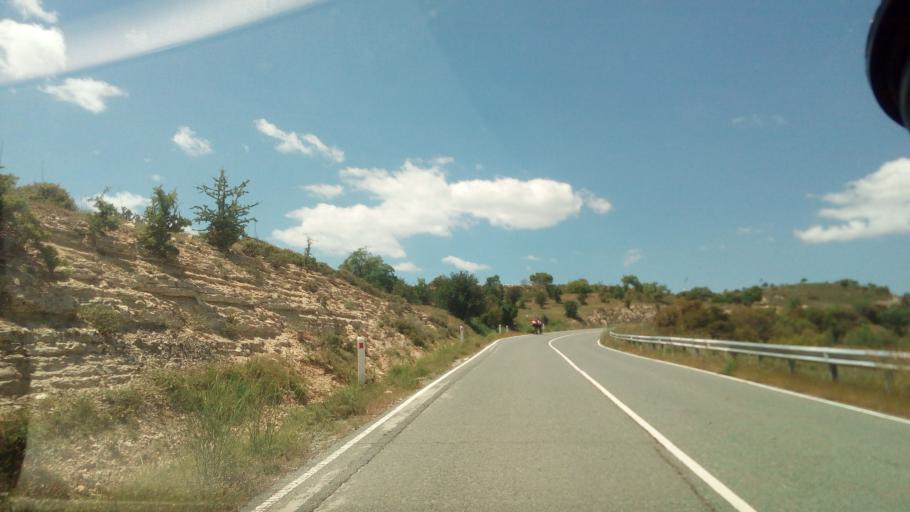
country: CY
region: Limassol
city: Pachna
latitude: 34.8184
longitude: 32.7742
